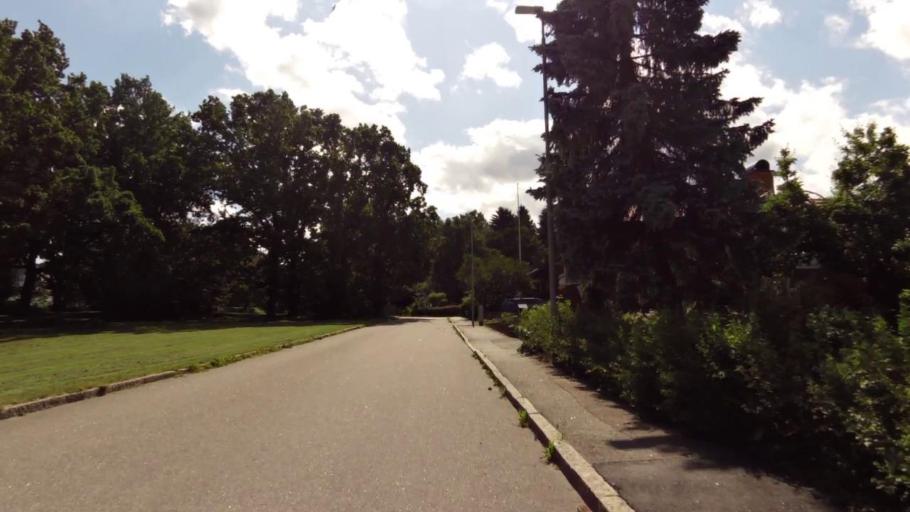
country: SE
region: OEstergoetland
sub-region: Linkopings Kommun
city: Linkoping
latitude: 58.4181
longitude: 15.5888
